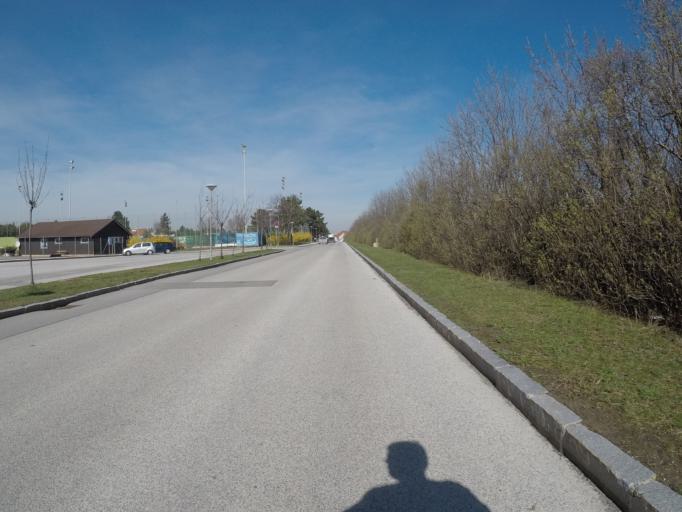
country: AT
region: Lower Austria
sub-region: Politischer Bezirk Modling
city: Vosendorf
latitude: 48.1159
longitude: 16.3369
